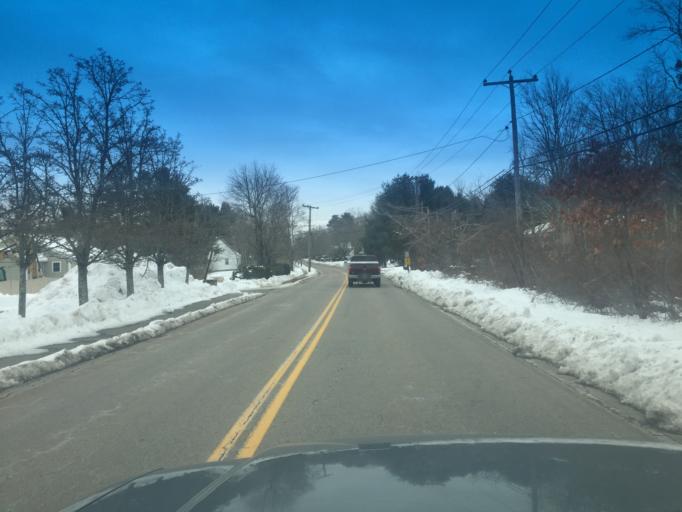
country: US
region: Massachusetts
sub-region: Norfolk County
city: Millis
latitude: 42.1620
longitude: -71.3659
